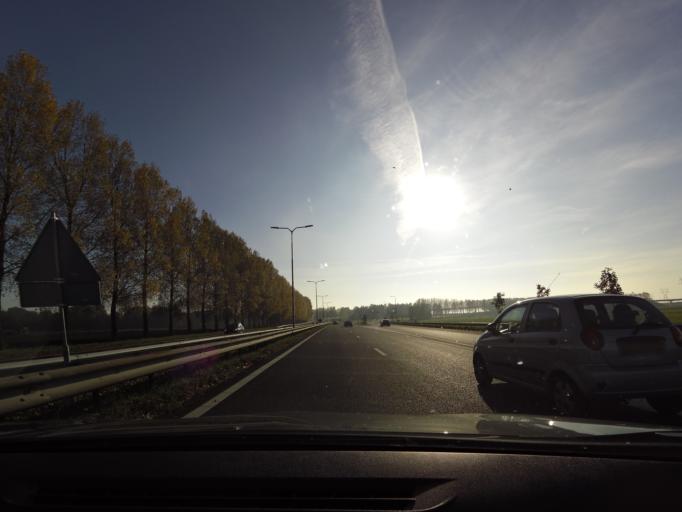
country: NL
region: South Holland
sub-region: Gemeente Ridderkerk
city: Ridderkerk
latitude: 51.8809
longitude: 4.5795
